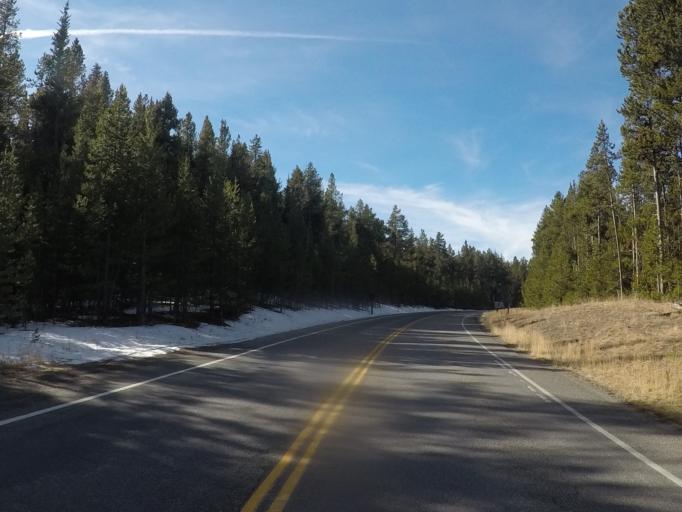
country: US
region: Montana
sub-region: Gallatin County
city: West Yellowstone
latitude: 44.5505
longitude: -110.4099
